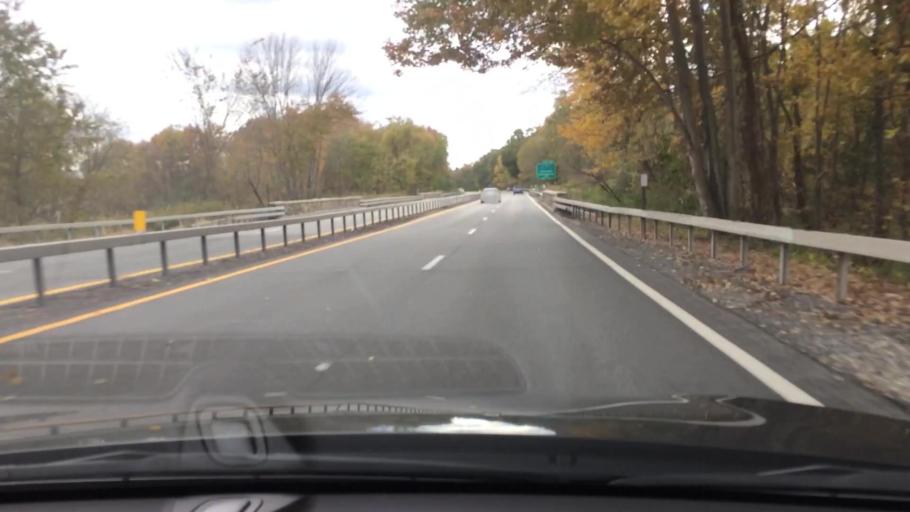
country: US
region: New York
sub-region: Dutchess County
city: Hillside Lake
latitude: 41.6455
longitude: -73.7884
